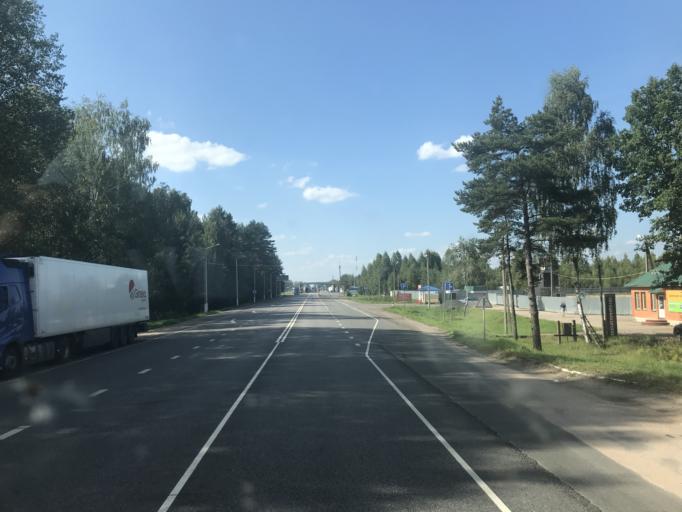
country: RU
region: Smolensk
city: Rudnya
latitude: 54.9863
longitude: 30.9607
